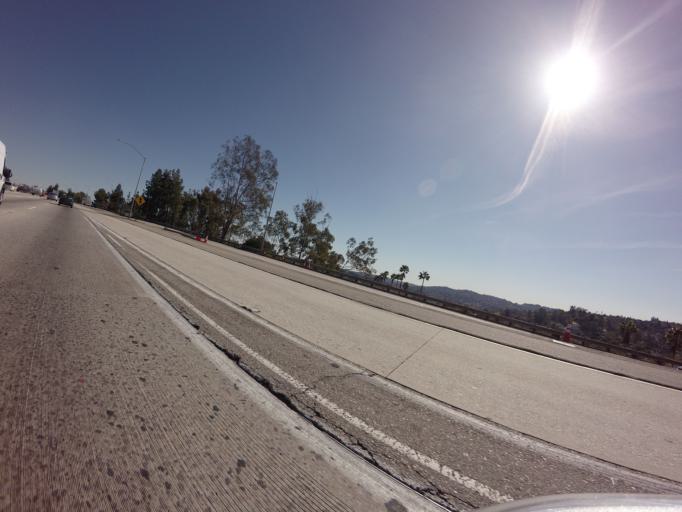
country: US
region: California
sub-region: Los Angeles County
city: Glendale
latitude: 34.1451
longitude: -118.2195
